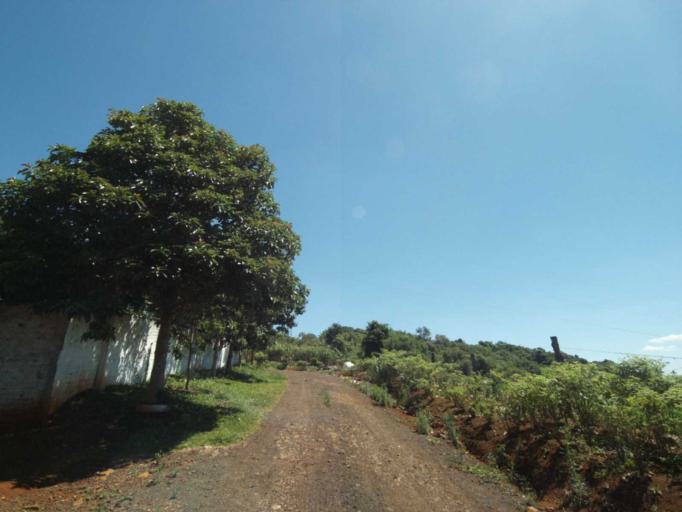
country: BR
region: Parana
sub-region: Laranjeiras Do Sul
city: Laranjeiras do Sul
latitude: -25.3868
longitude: -52.2151
